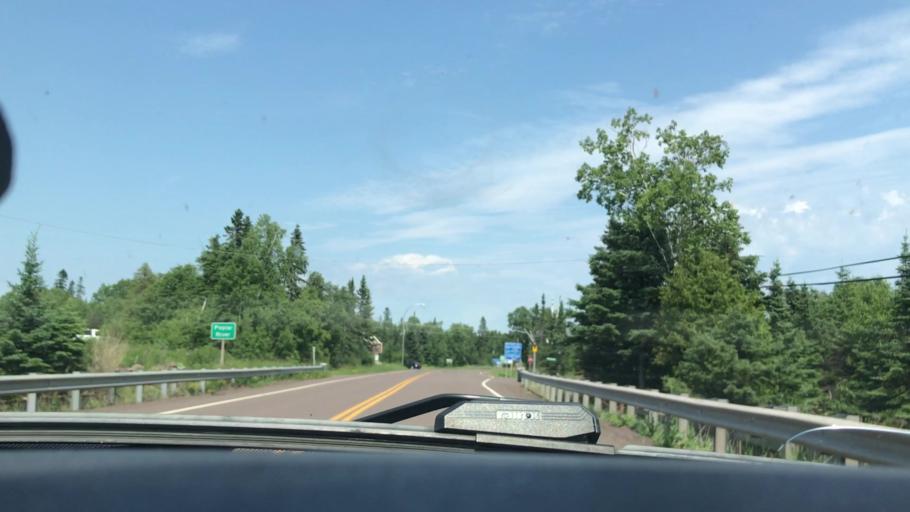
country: US
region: Minnesota
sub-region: Cook County
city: Grand Marais
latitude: 47.6388
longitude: -90.7081
